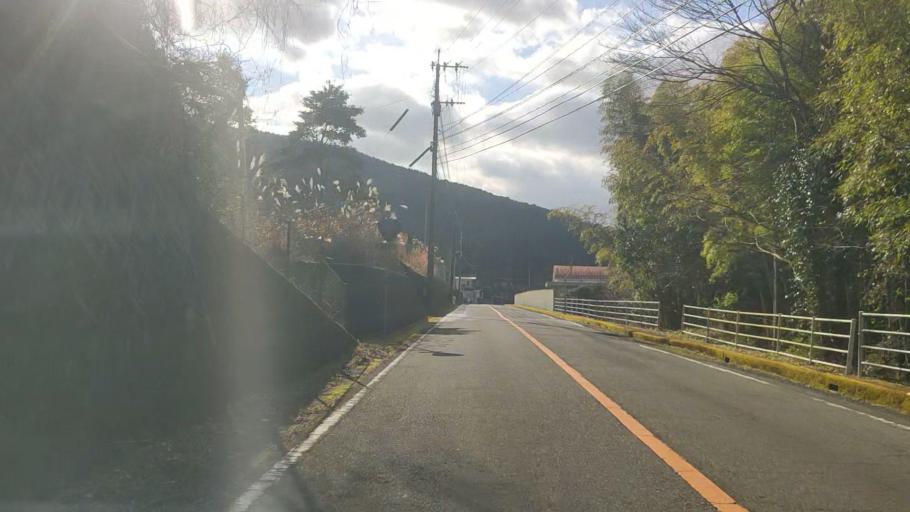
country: JP
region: Kumamoto
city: Hitoyoshi
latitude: 32.3092
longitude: 130.8477
